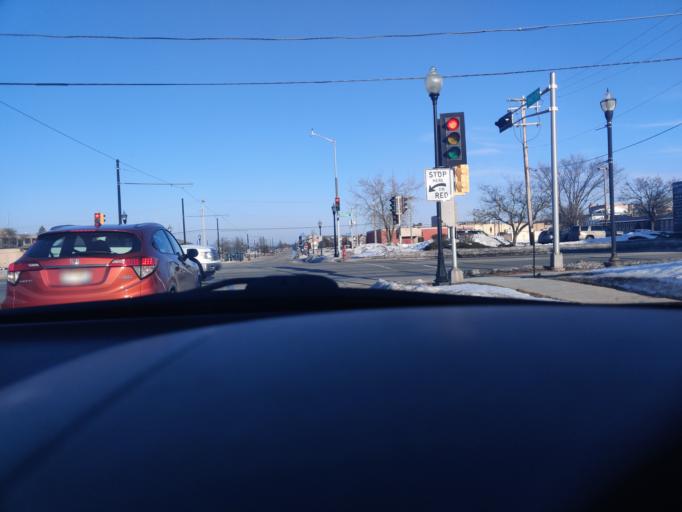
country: US
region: Wisconsin
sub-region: Kenosha County
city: Kenosha
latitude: 42.5864
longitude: -87.8229
